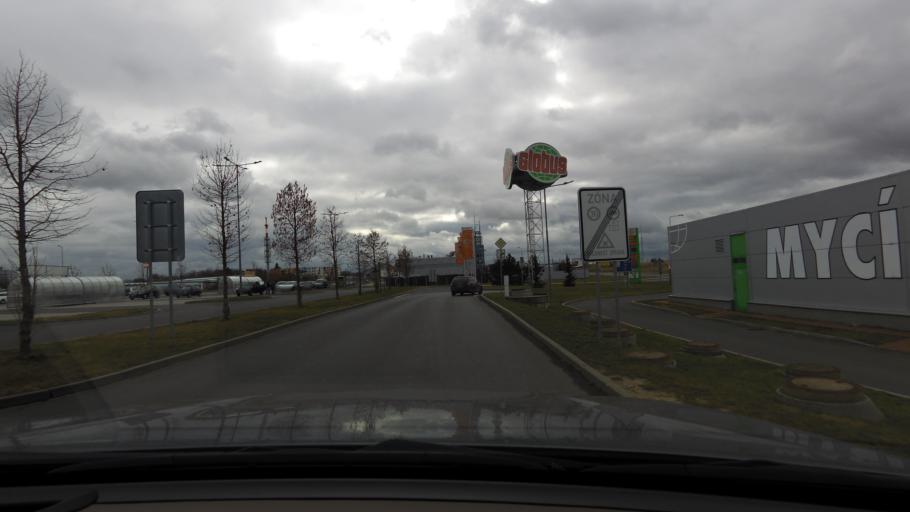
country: CZ
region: Plzensky
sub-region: Okres Plzen-Mesto
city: Pilsen
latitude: 49.7766
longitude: 13.3470
